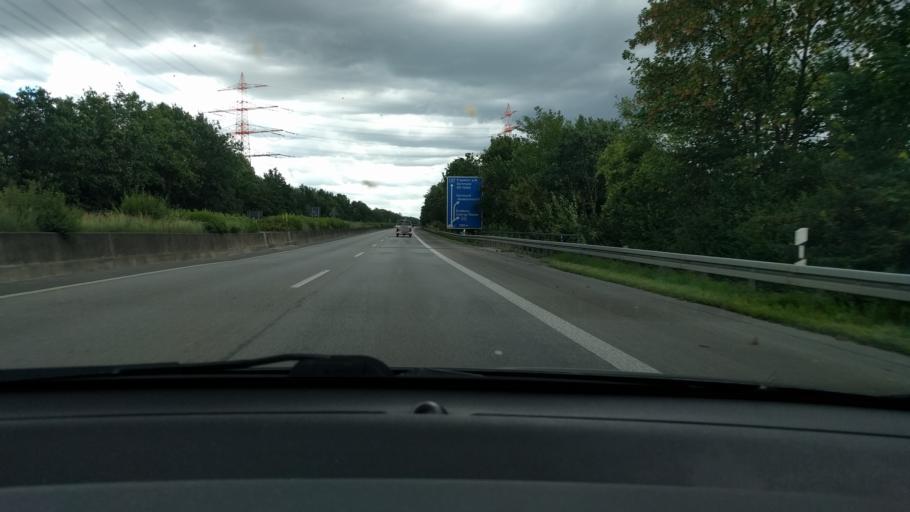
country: DE
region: North Rhine-Westphalia
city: Castrop-Rauxel
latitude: 51.5771
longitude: 7.3648
